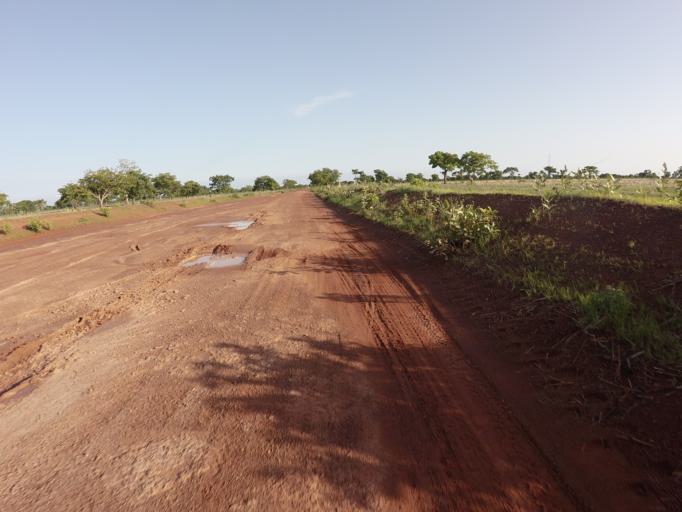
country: TG
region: Savanes
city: Sansanne-Mango
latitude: 10.3745
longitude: -0.0944
